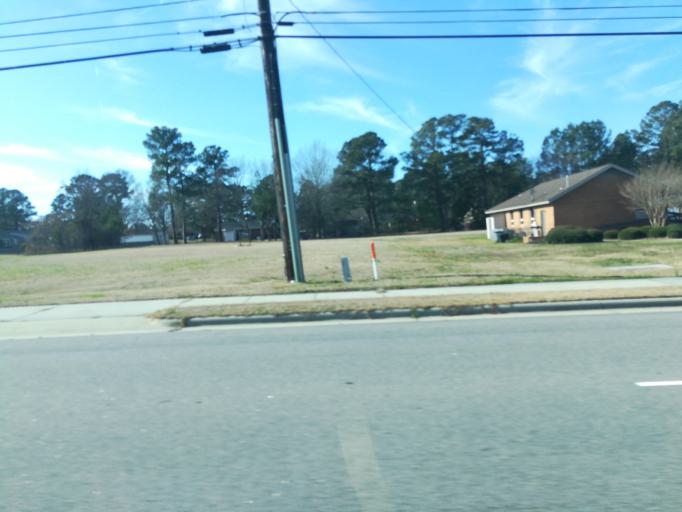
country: US
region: North Carolina
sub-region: Nash County
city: Rocky Mount
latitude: 35.9660
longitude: -77.8498
